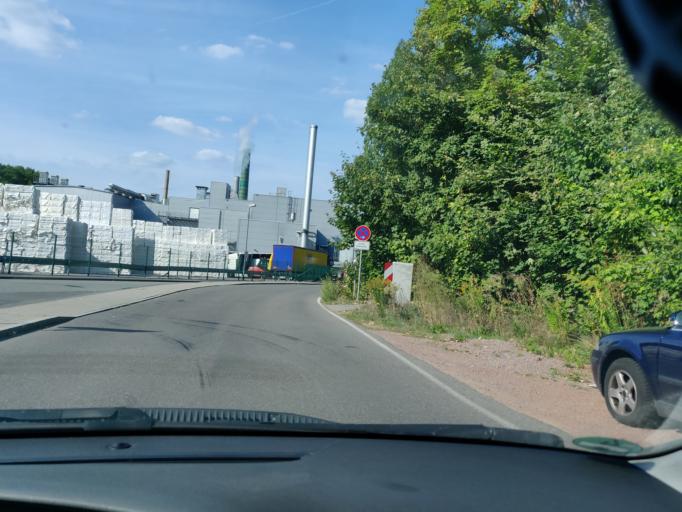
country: DE
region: Saxony
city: Kriebstein
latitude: 51.0454
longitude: 13.0184
